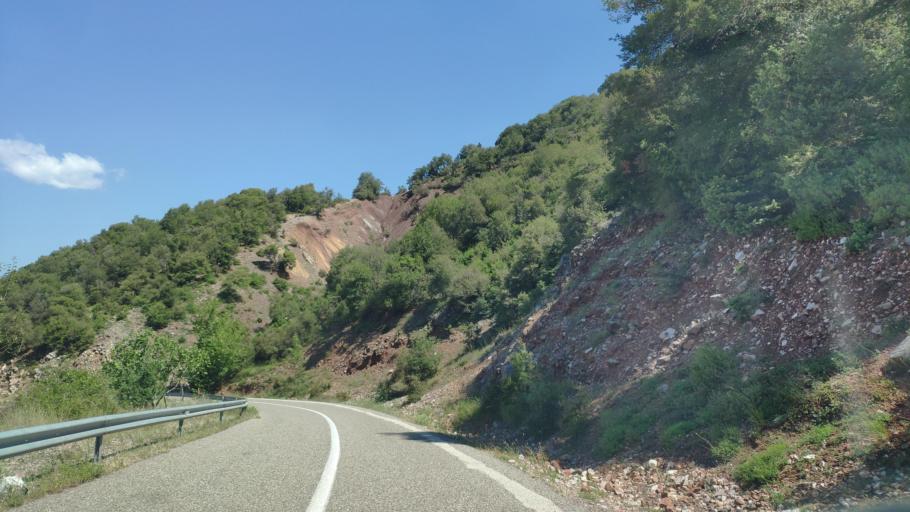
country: GR
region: Central Greece
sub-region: Nomos Evrytanias
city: Kerasochori
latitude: 39.0063
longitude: 21.5960
